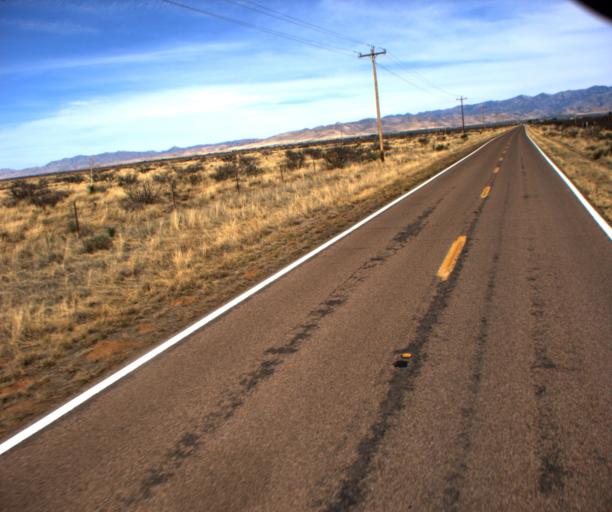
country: US
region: Arizona
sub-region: Cochise County
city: Willcox
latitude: 31.8762
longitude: -109.5949
